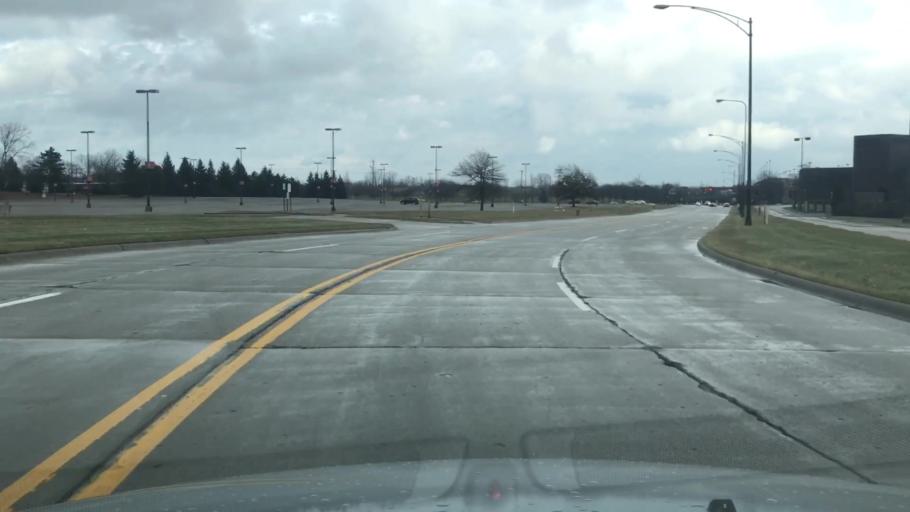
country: US
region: Michigan
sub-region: Oakland County
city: Birmingham
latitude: 42.5643
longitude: -83.1913
